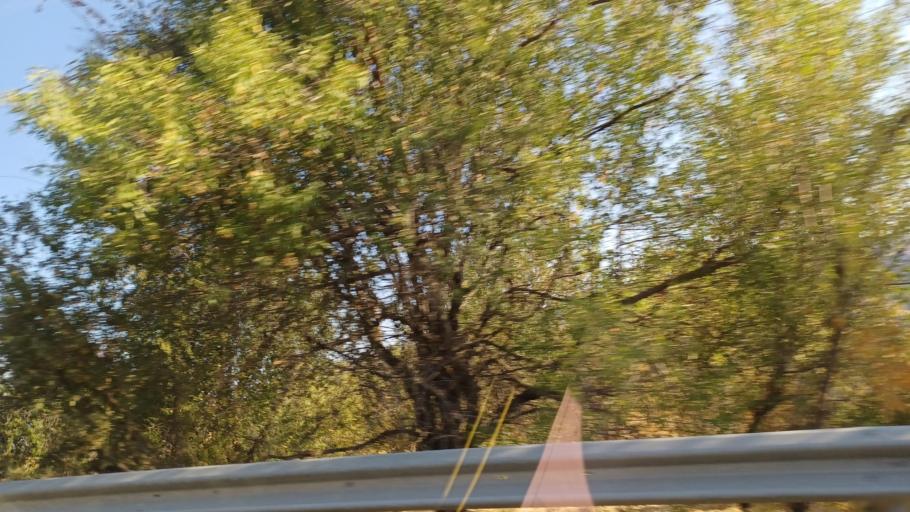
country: CY
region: Pafos
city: Polis
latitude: 34.9467
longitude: 32.5035
